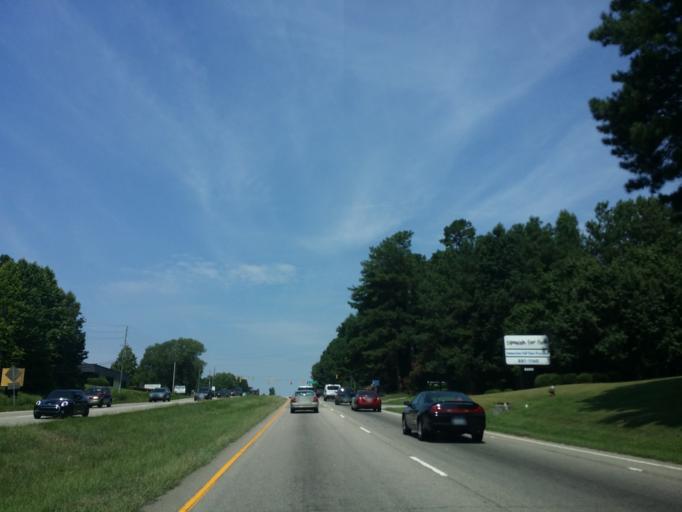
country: US
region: North Carolina
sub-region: Wake County
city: Cary
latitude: 35.8724
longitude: -78.7259
